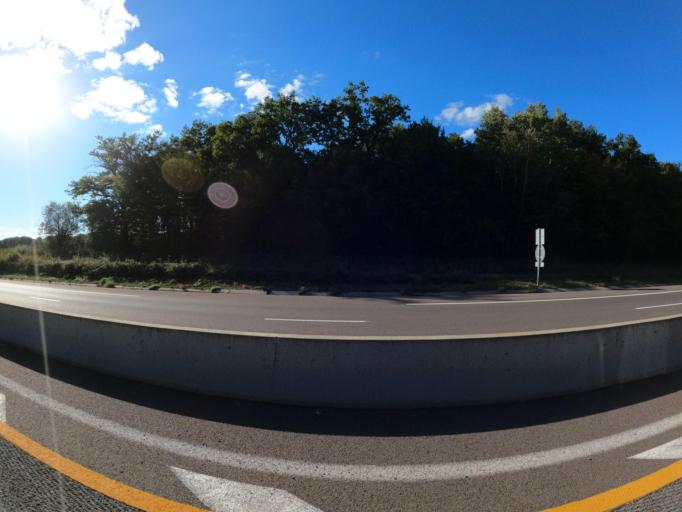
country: FR
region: Bourgogne
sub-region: Departement de Saone-et-Loire
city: Genelard
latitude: 46.5984
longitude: 4.2403
